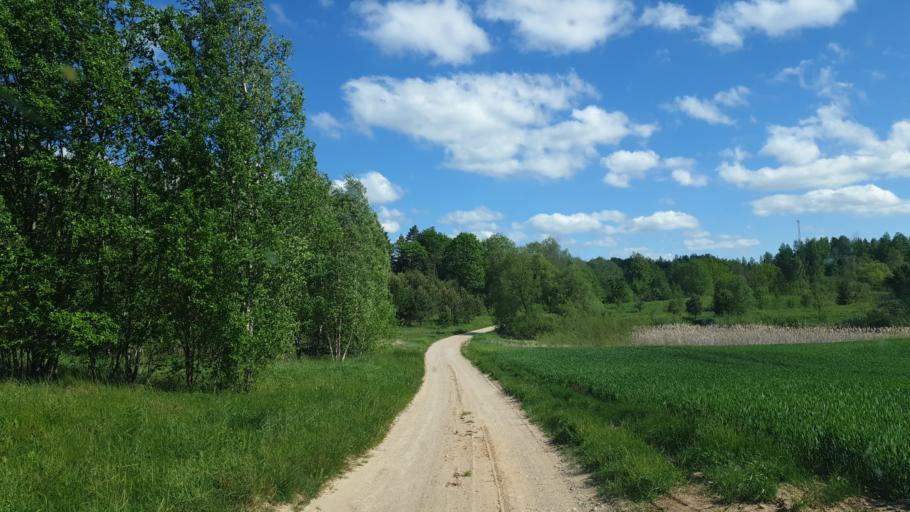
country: LT
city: Aukstadvaris
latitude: 54.5784
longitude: 24.4598
